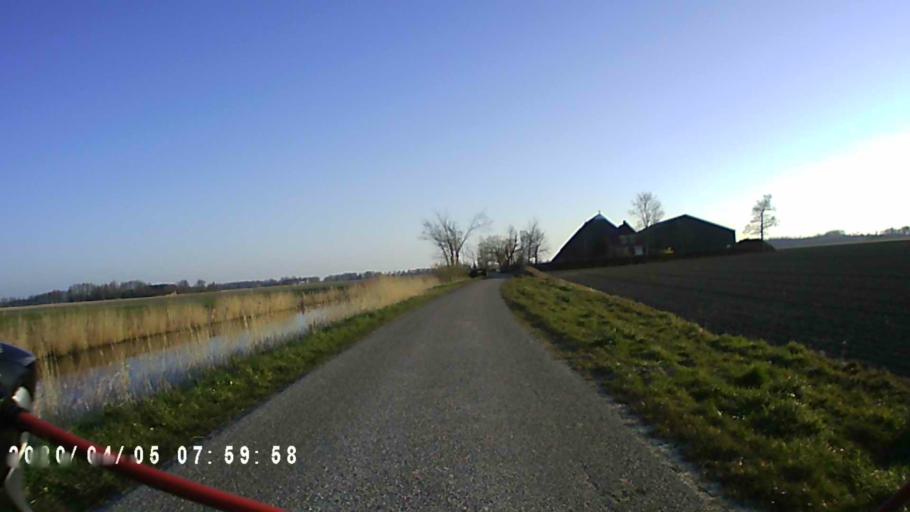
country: NL
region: Groningen
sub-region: Gemeente Zuidhorn
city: Oldehove
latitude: 53.3419
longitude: 6.4316
